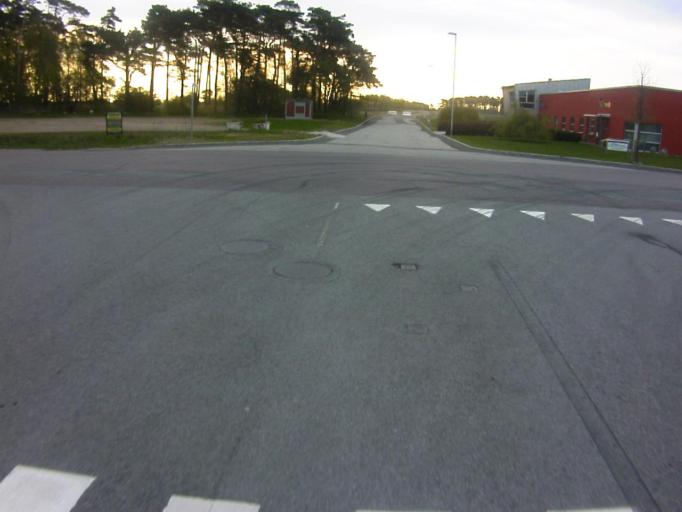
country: SE
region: Skane
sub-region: Kavlinge Kommun
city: Loddekopinge
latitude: 55.7684
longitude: 12.9977
